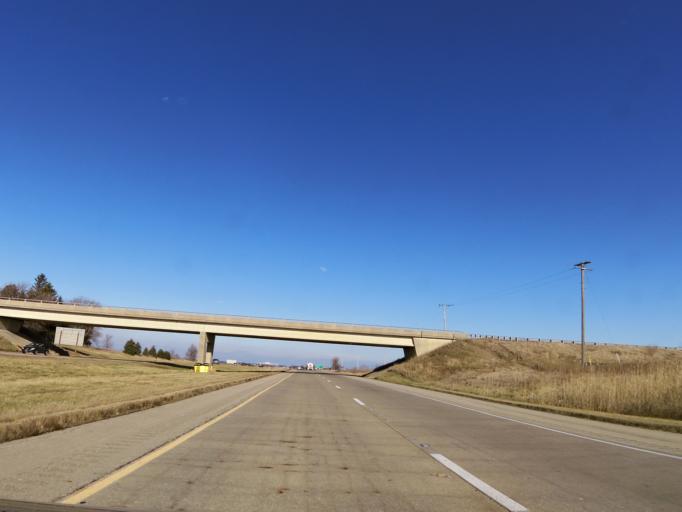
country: US
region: Illinois
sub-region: LaSalle County
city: La Salle
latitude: 41.3820
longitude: -89.0577
